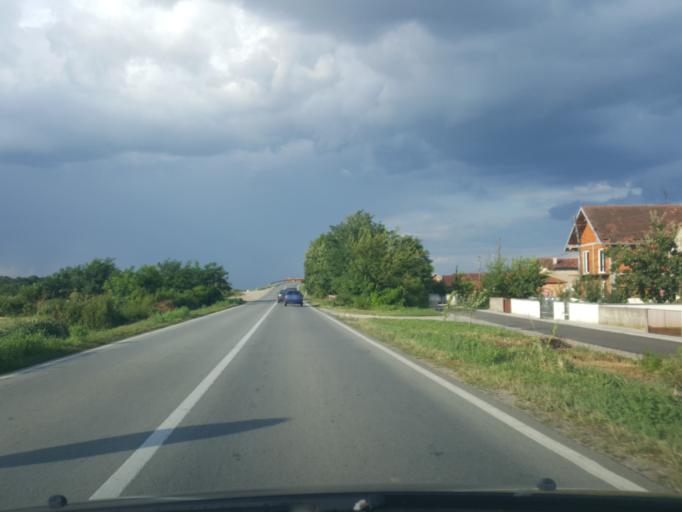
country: RS
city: Lesnica
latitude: 44.6590
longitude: 19.3232
